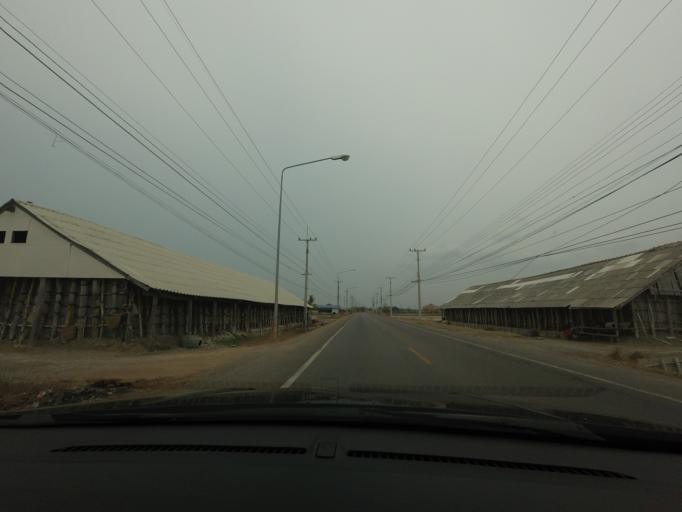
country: TH
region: Phetchaburi
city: Ban Laem
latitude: 13.2237
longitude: 99.9742
